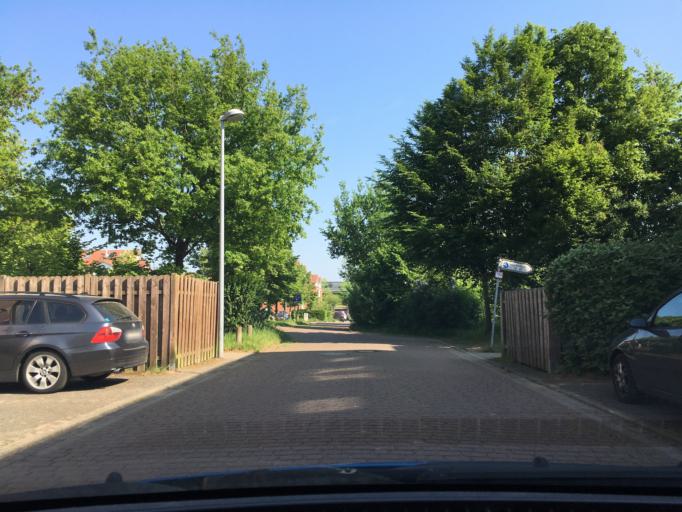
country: DE
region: Lower Saxony
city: Lueneburg
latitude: 53.2260
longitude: 10.4010
